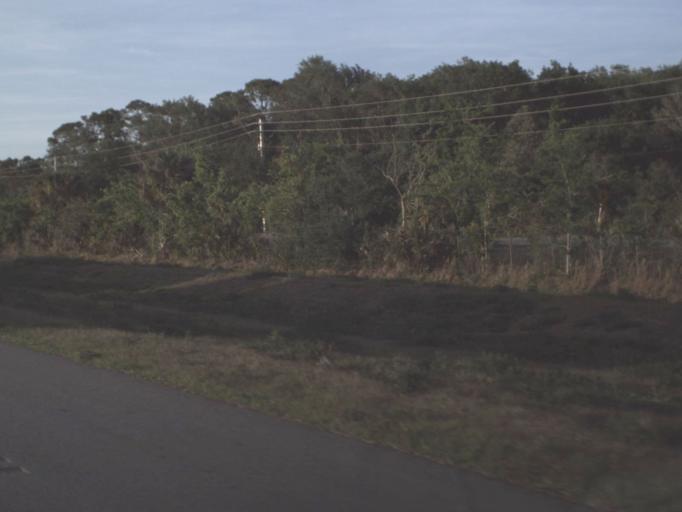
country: US
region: Florida
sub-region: Brevard County
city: Mims
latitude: 28.6497
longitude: -80.8628
